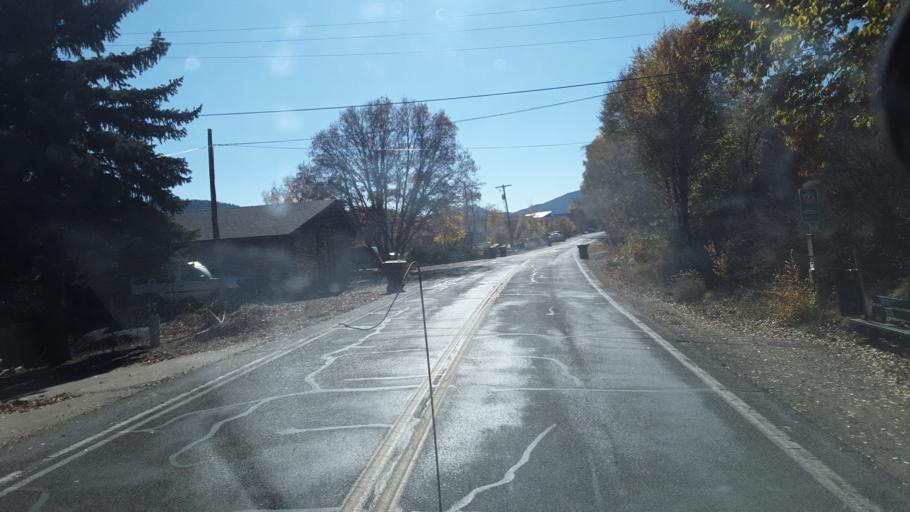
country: US
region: Colorado
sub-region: La Plata County
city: Durango
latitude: 37.3124
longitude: -107.8539
